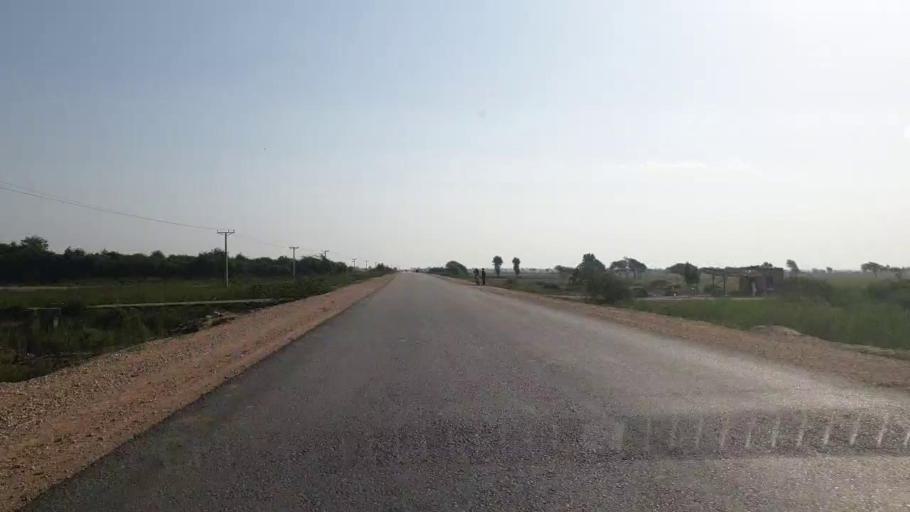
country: PK
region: Sindh
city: Tando Bago
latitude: 24.6575
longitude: 68.9918
